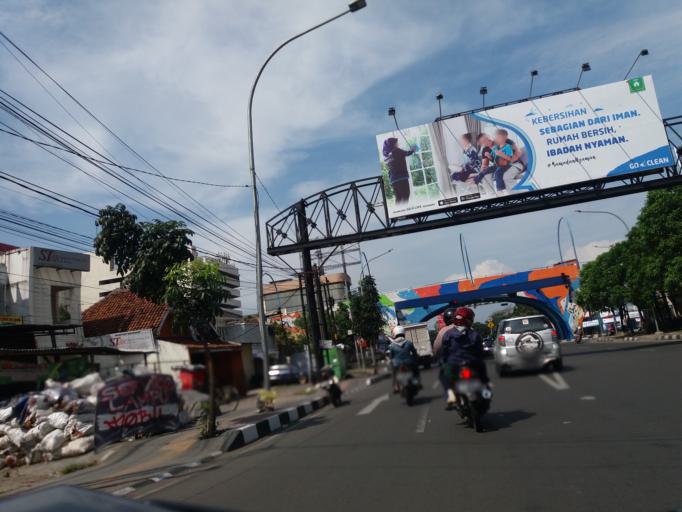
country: ID
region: West Java
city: Bandung
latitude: -6.9126
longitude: 107.6436
